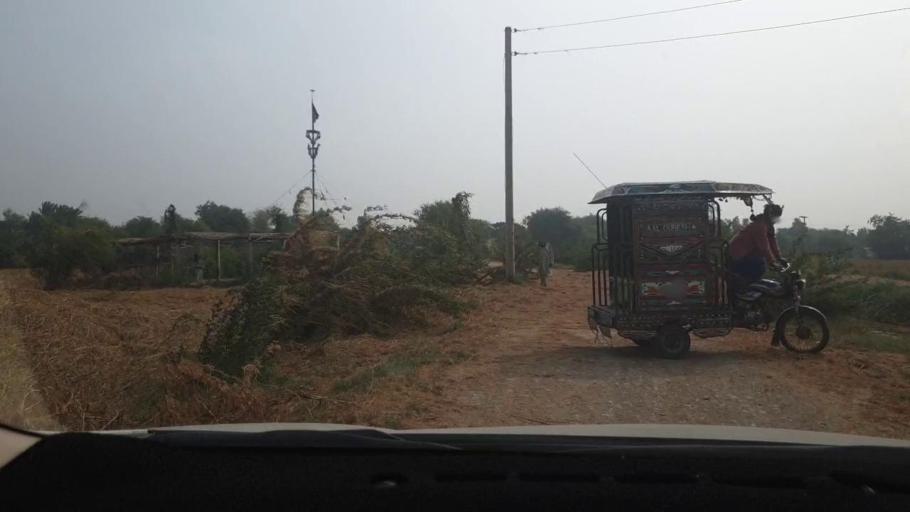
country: PK
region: Sindh
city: Tando Muhammad Khan
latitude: 25.0609
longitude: 68.5073
